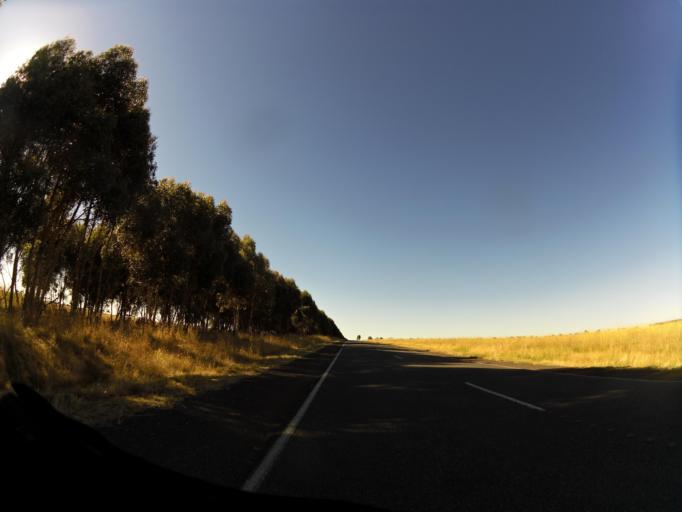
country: AU
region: Victoria
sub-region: Ballarat North
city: Delacombe
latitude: -37.6494
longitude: 143.3485
